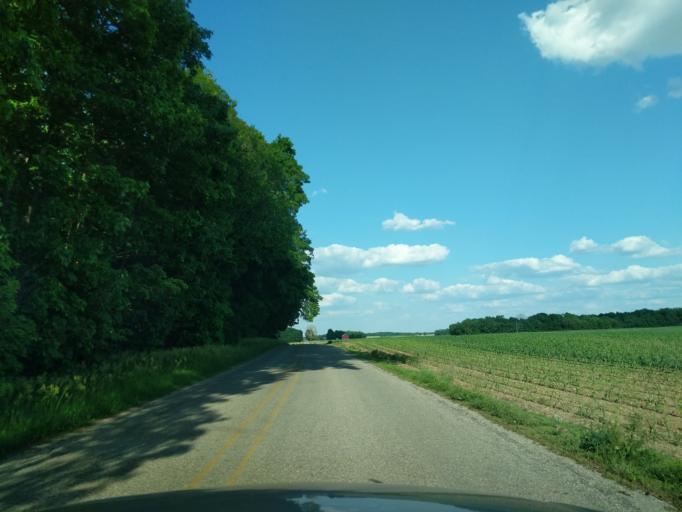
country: US
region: Indiana
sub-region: Kosciusko County
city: North Webster
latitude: 41.3024
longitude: -85.6331
